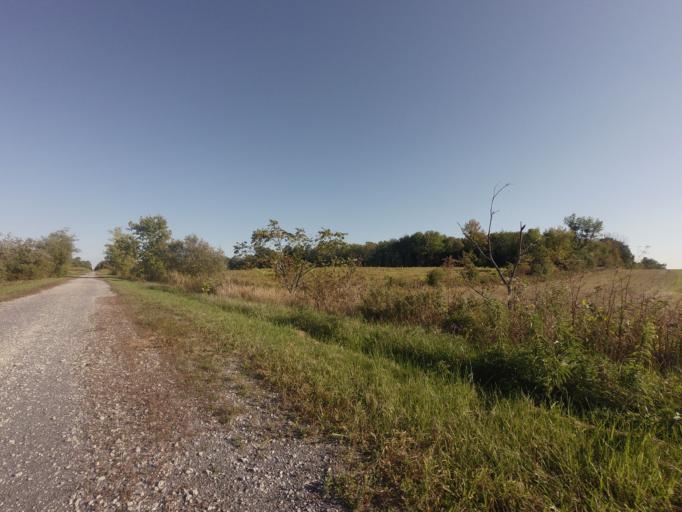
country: CA
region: Ontario
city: Hawkesbury
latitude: 45.5315
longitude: -74.5757
